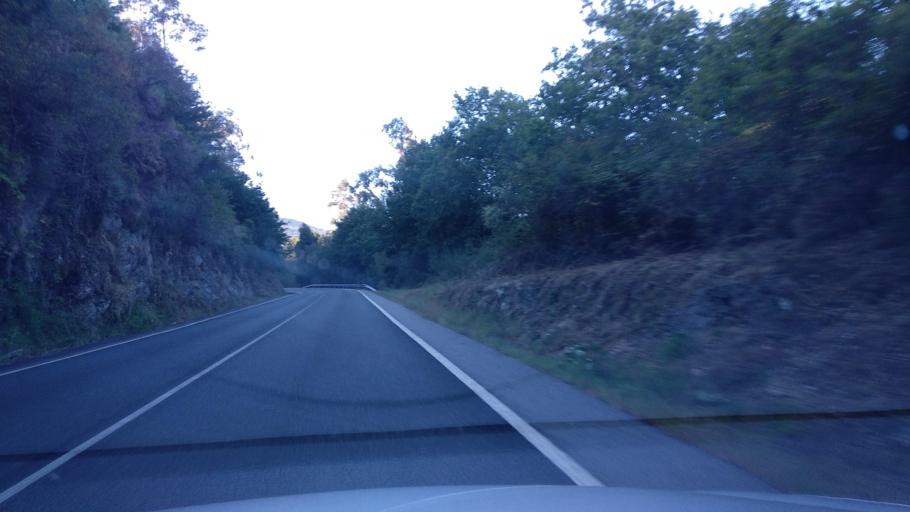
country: ES
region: Galicia
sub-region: Provincia de Pontevedra
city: Ponte Caldelas
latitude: 42.3413
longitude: -8.5575
